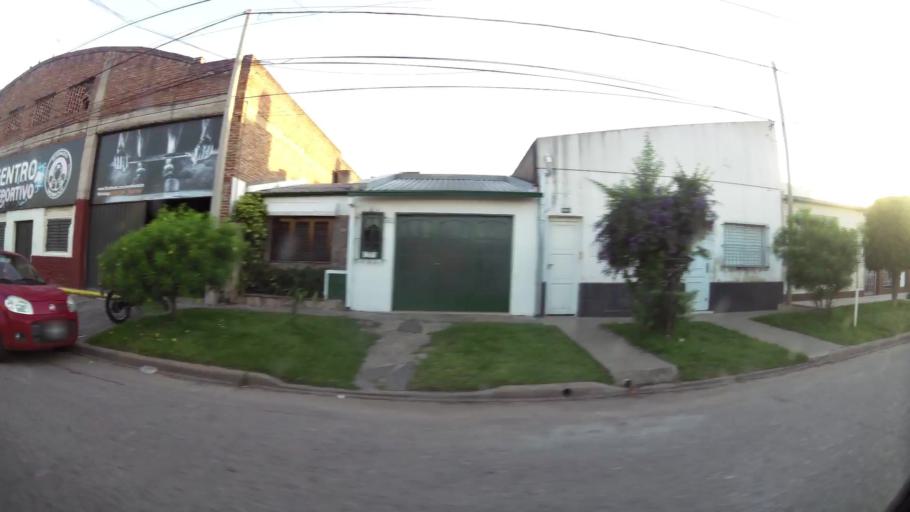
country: AR
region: Santa Fe
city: Santa Fe de la Vera Cruz
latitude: -31.6036
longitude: -60.6854
